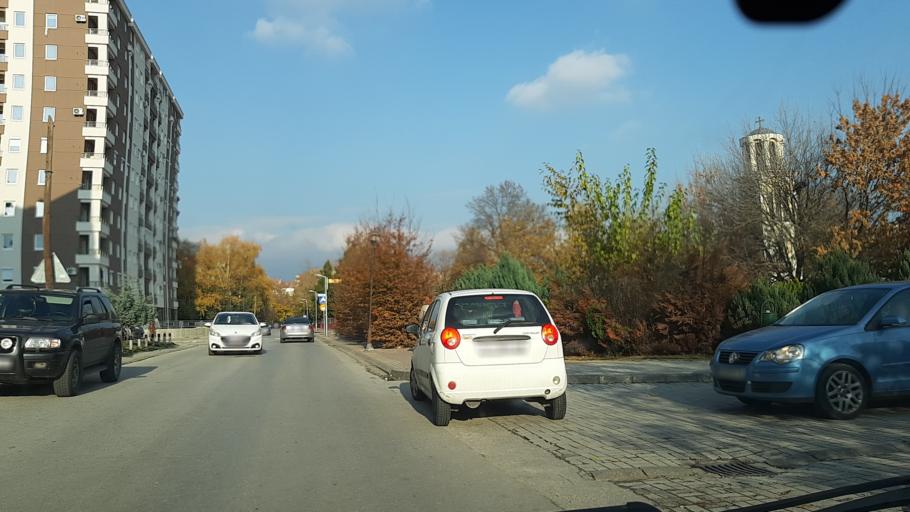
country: MK
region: Kisela Voda
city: Usje
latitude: 41.9857
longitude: 21.4571
